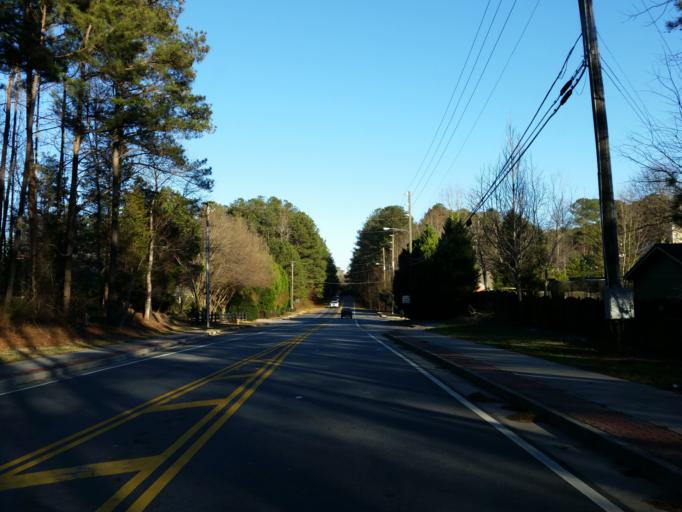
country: US
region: Georgia
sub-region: Cobb County
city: Acworth
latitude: 33.9756
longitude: -84.7121
